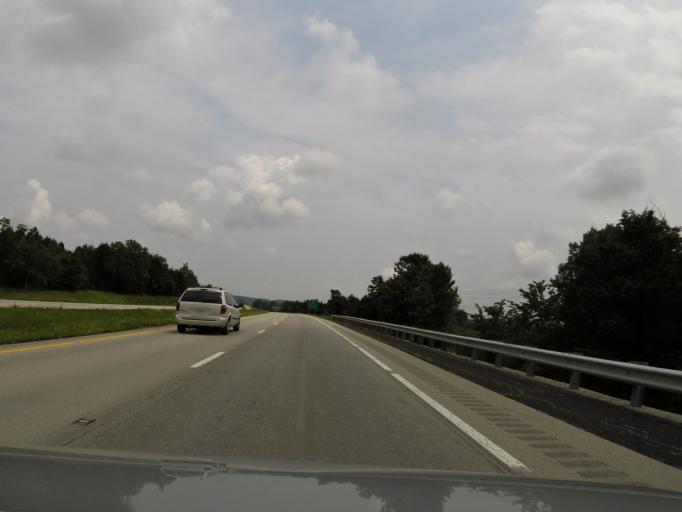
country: US
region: Kentucky
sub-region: Hardin County
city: Elizabethtown
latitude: 37.5641
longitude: -86.0546
